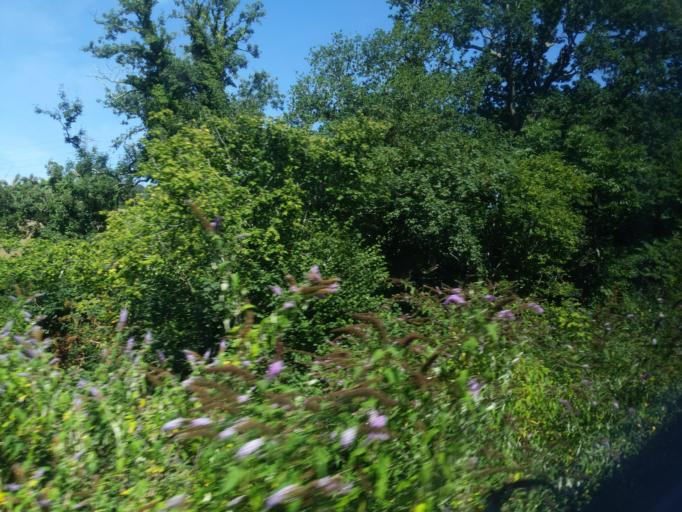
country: GB
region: England
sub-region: Devon
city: Plympton
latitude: 50.3934
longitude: -4.0180
